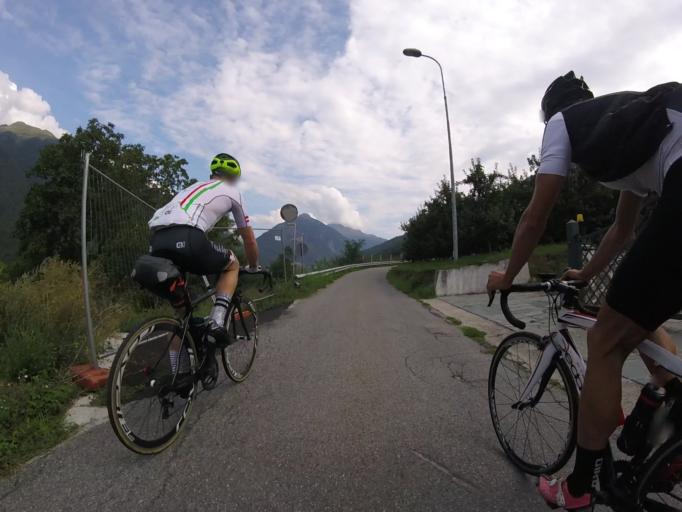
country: IT
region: Lombardy
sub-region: Provincia di Sondrio
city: Mazzo di Valtellina
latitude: 46.2519
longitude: 10.2563
